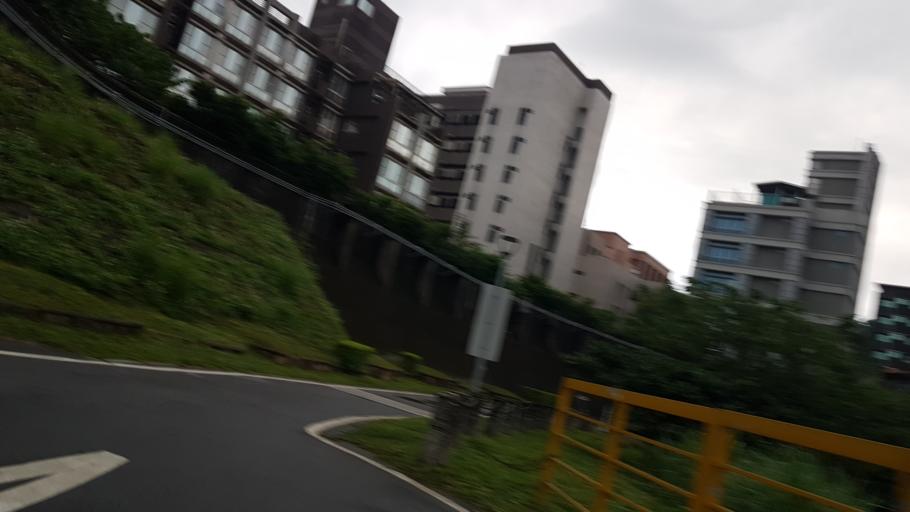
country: TW
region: Taipei
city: Taipei
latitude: 24.9864
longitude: 121.5507
